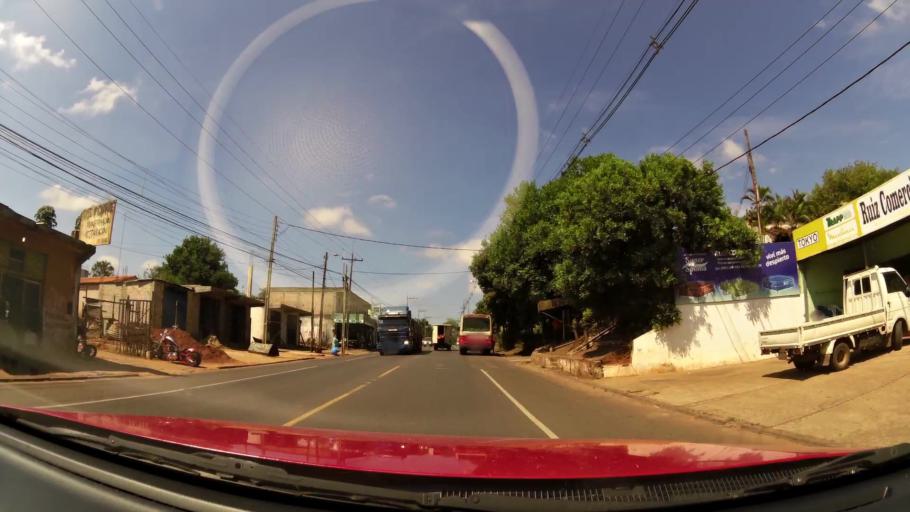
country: PY
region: Central
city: San Lorenzo
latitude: -25.3105
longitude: -57.5060
